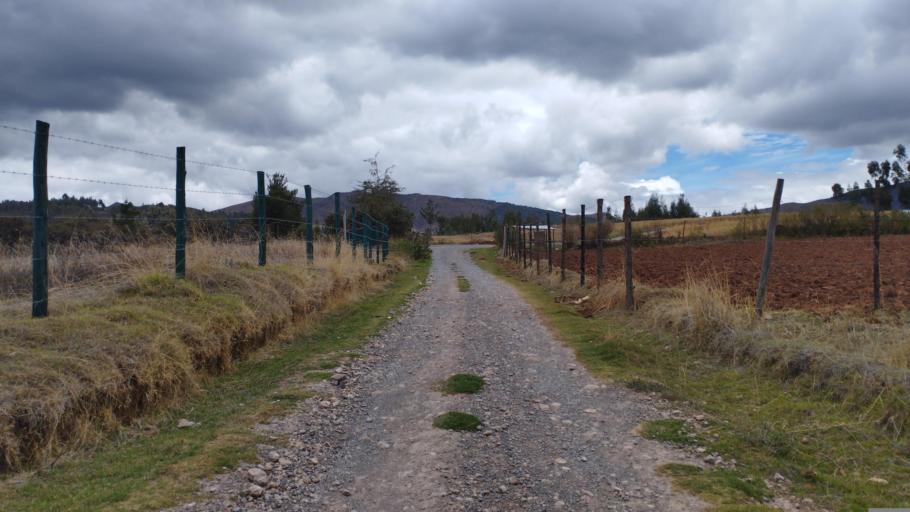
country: PE
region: Cusco
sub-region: Provincia de Cusco
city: Cusco
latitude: -13.5134
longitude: -71.9420
